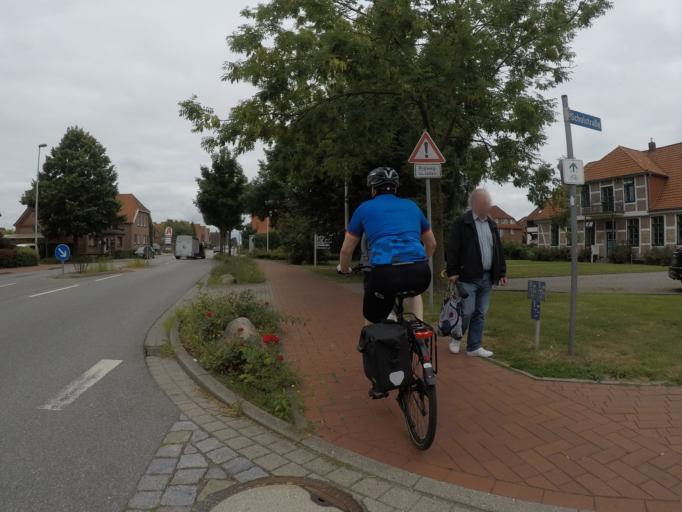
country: DE
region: Lower Saxony
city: Jork
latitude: 53.5336
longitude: 9.6772
